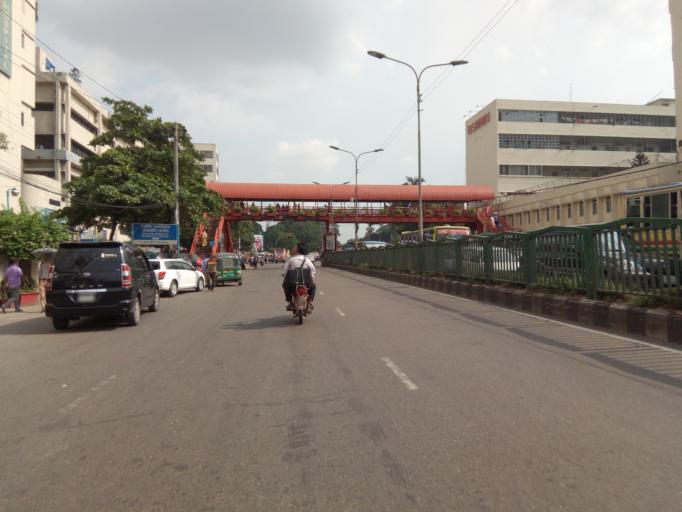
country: BD
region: Dhaka
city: Azimpur
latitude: 23.7396
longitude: 90.3961
